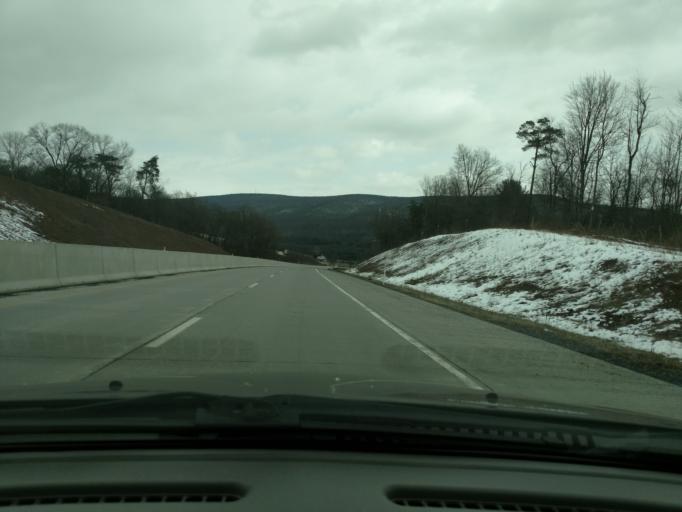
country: US
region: Pennsylvania
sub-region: Schuylkill County
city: Orwigsburg
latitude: 40.6150
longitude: -76.0408
